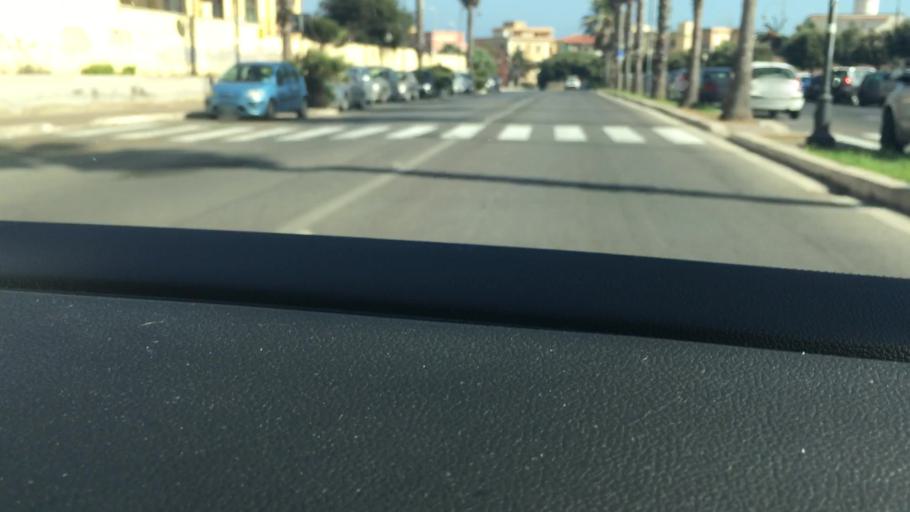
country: IT
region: Latium
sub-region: Citta metropolitana di Roma Capitale
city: Anzio
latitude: 41.4471
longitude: 12.6206
